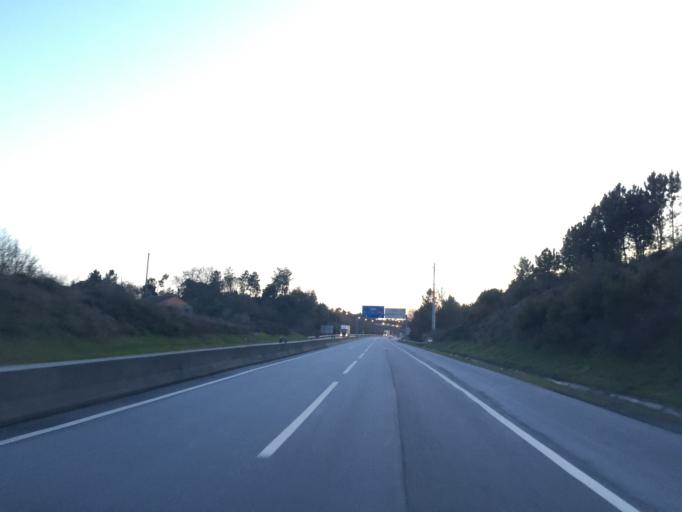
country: PT
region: Viseu
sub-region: Concelho de Carregal do Sal
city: Carregal do Sal
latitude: 40.4341
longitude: -8.0141
